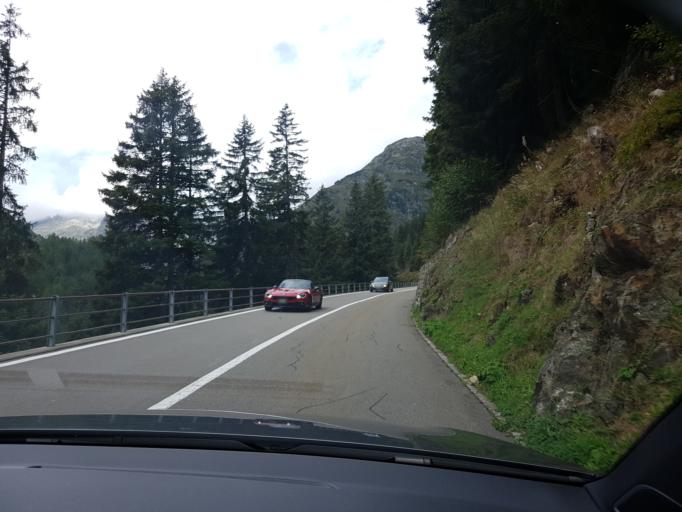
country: CH
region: Uri
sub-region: Uri
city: Andermatt
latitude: 46.7376
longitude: 8.5175
